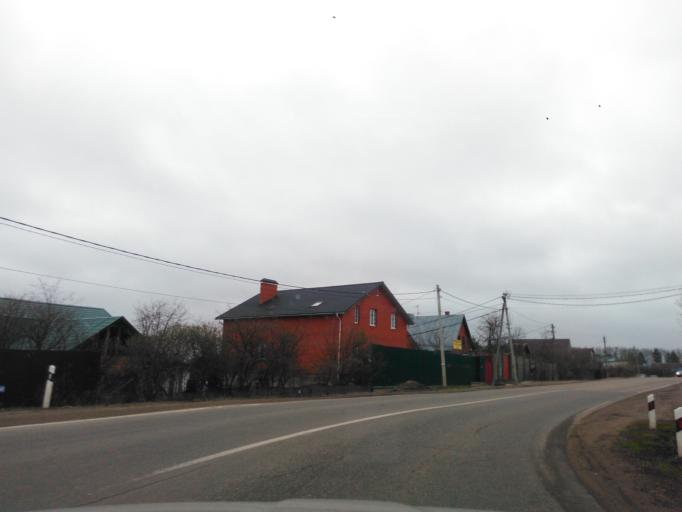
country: RU
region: Moskovskaya
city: Nakhabino
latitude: 55.8308
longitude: 37.1465
